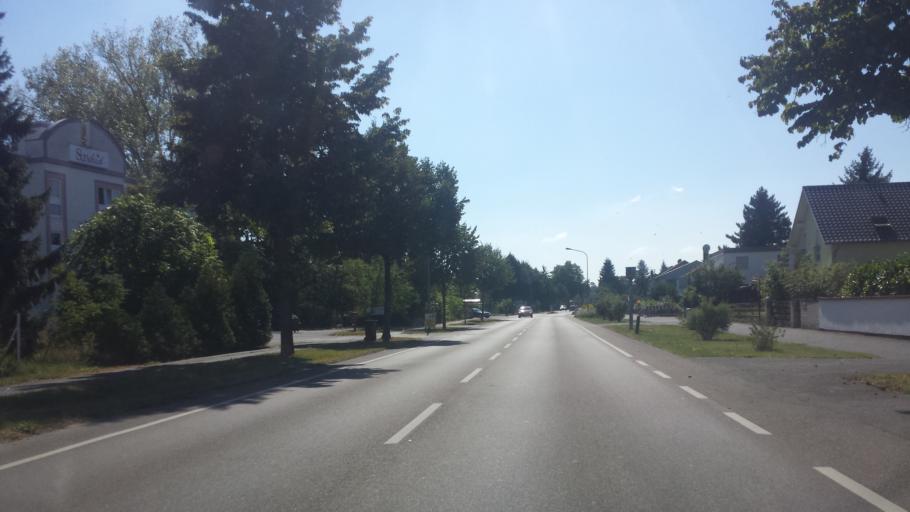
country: DE
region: Hesse
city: Lorsch
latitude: 49.6432
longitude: 8.5681
